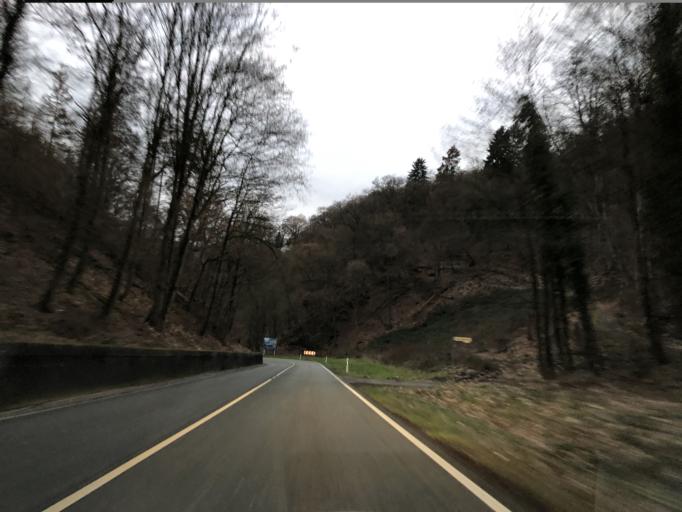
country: DE
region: Rheinland-Pfalz
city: Bad Ems
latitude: 50.3421
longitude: 7.7047
